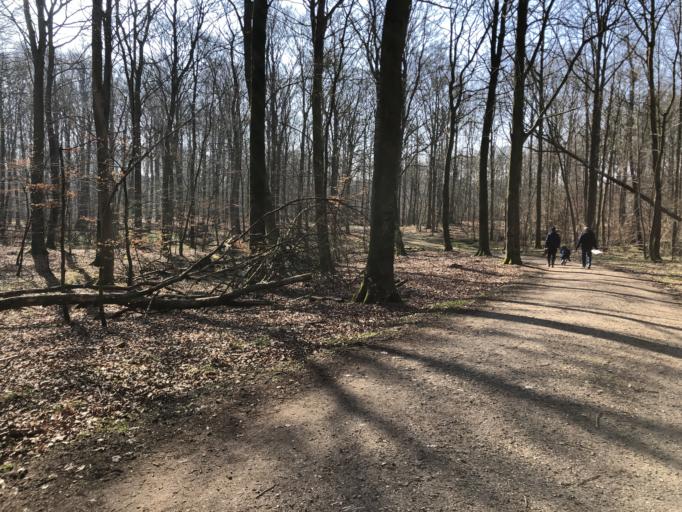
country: DK
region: Capital Region
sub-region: Allerod Kommune
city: Blovstrod
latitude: 55.9000
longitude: 12.3902
